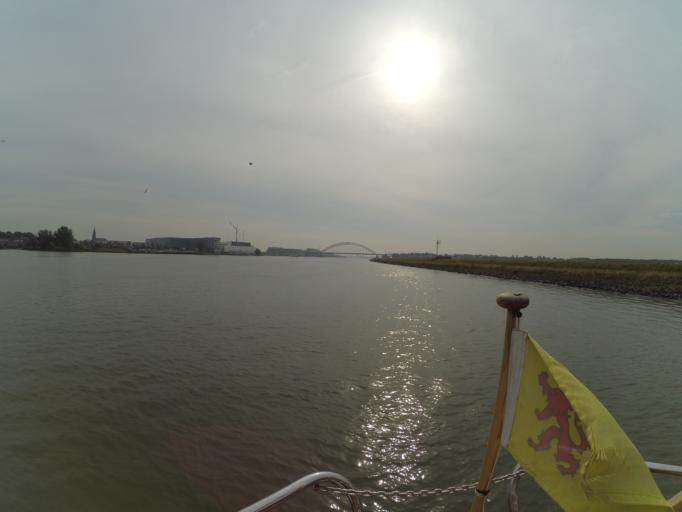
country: NL
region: South Holland
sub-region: Gemeente Alblasserdam
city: Alblasserdam
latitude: 51.8629
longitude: 4.6460
